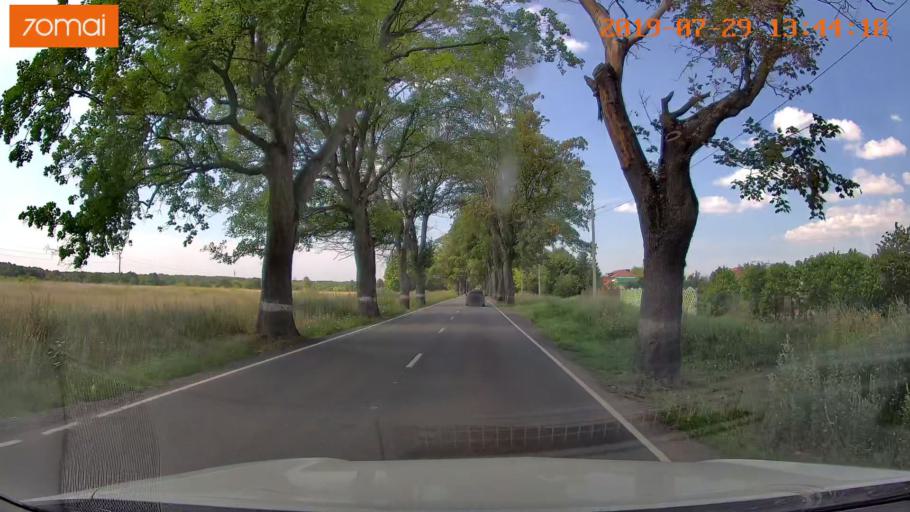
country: RU
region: Kaliningrad
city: Svetlyy
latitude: 54.7375
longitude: 20.0902
